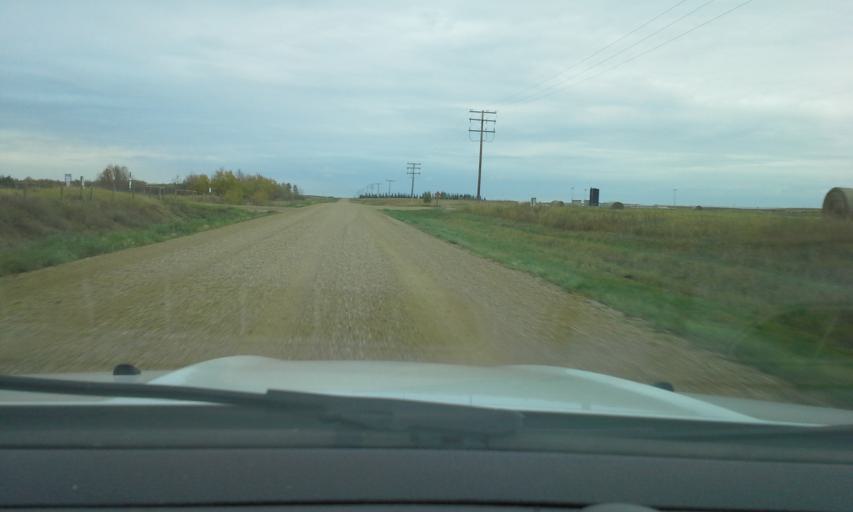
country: CA
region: Saskatchewan
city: Lloydminster
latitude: 53.2962
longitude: -109.8085
